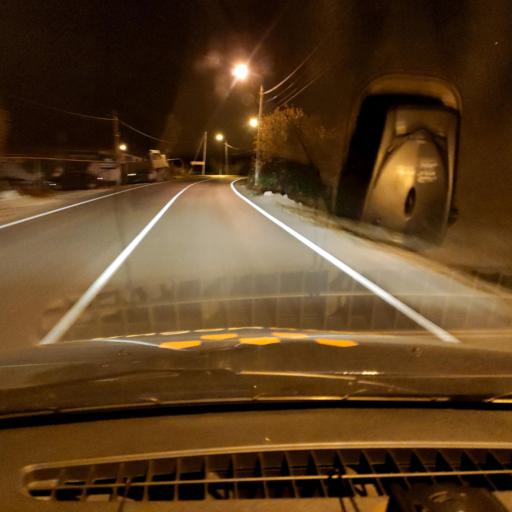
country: RU
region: Voronezj
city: Shilovo
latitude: 51.5787
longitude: 39.0375
